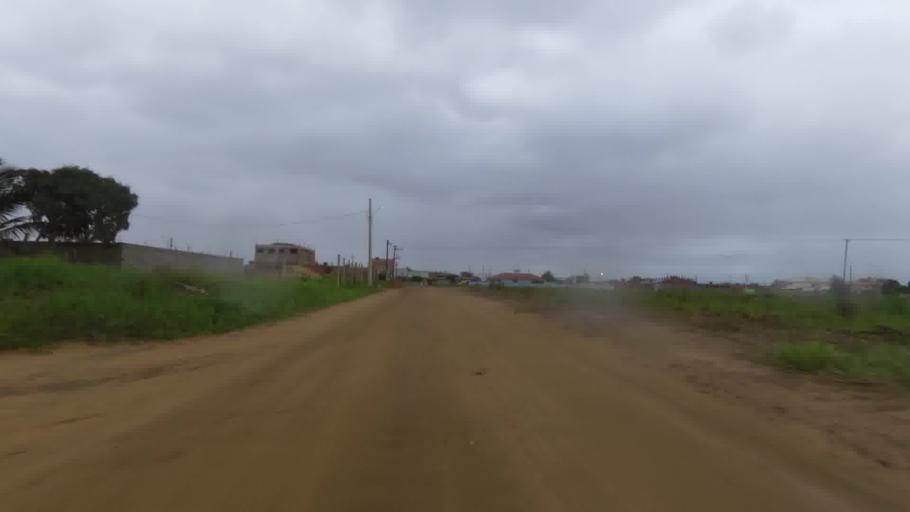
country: BR
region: Espirito Santo
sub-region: Marataizes
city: Marataizes
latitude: -21.0427
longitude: -40.8393
